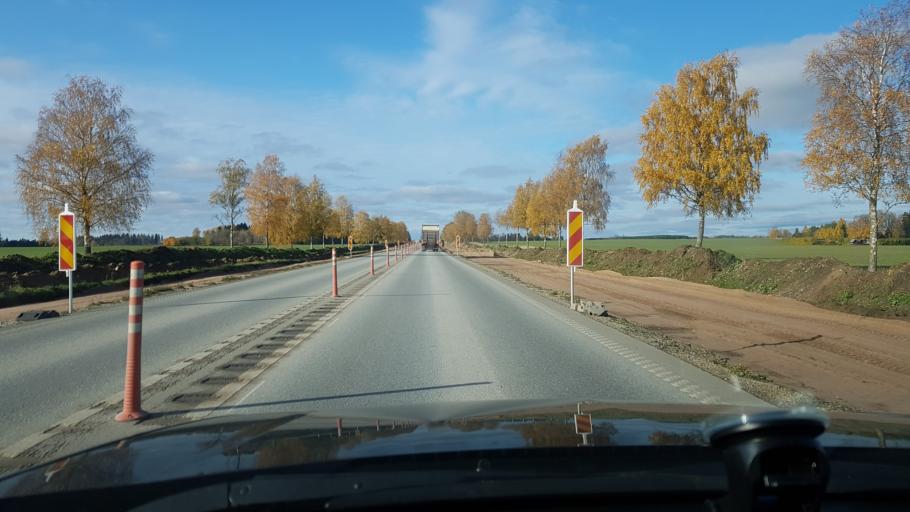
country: EE
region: Laeaene-Virumaa
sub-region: Haljala vald
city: Haljala
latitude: 59.4324
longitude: 26.1939
